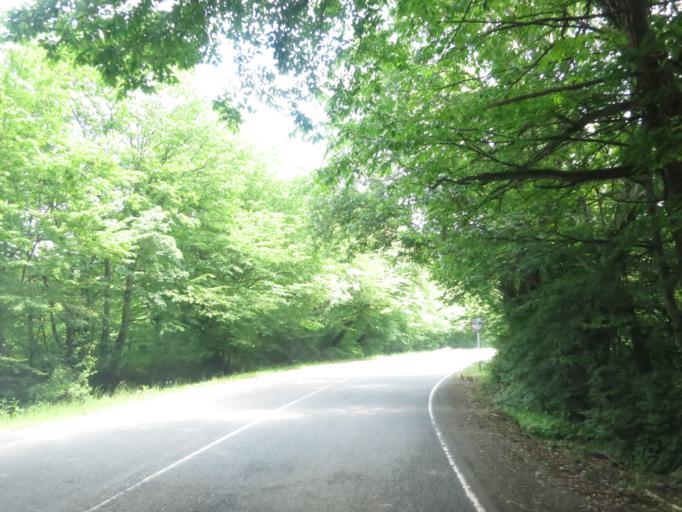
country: GE
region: Kakheti
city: Sagarejo
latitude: 41.8651
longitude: 45.3428
